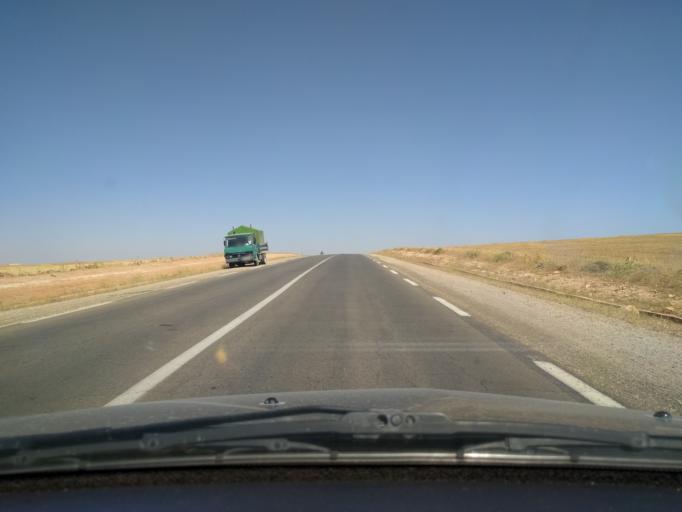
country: DZ
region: Tiaret
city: Frenda
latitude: 34.8841
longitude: 1.1889
